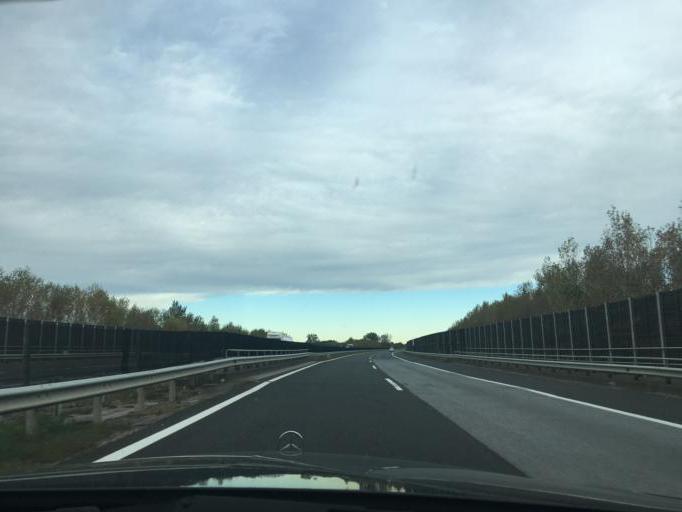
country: HU
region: Hajdu-Bihar
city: Polgar
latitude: 47.8500
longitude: 21.0638
